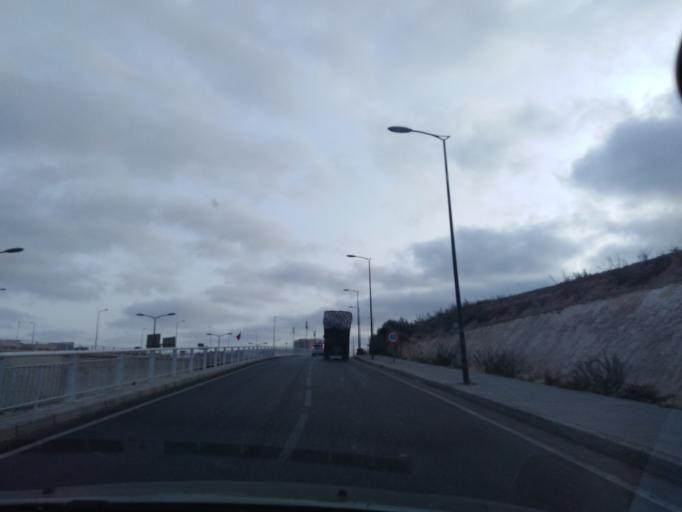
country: MA
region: Grand Casablanca
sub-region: Casablanca
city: Casablanca
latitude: 33.5471
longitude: -7.6471
